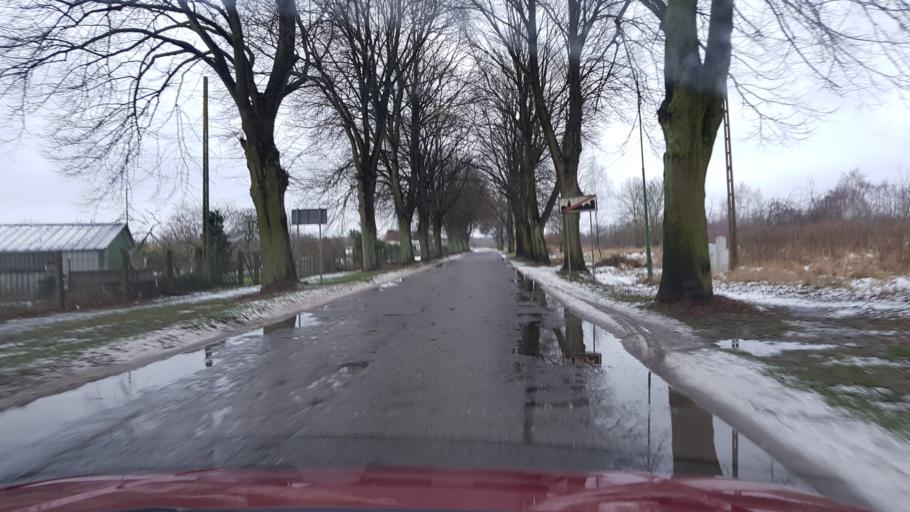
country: PL
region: West Pomeranian Voivodeship
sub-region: Powiat goleniowski
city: Nowogard
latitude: 53.6607
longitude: 15.1248
